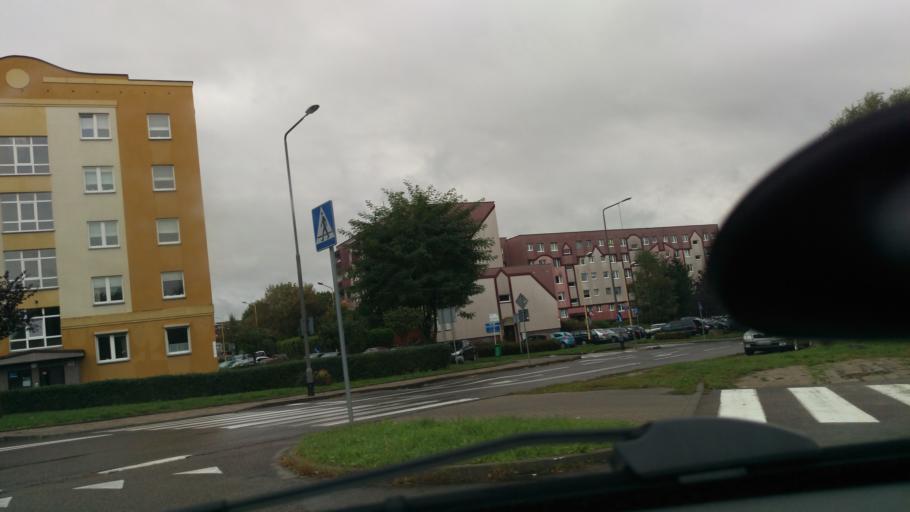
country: PL
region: West Pomeranian Voivodeship
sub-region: Szczecin
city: Szczecin
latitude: 53.3657
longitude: 14.6614
